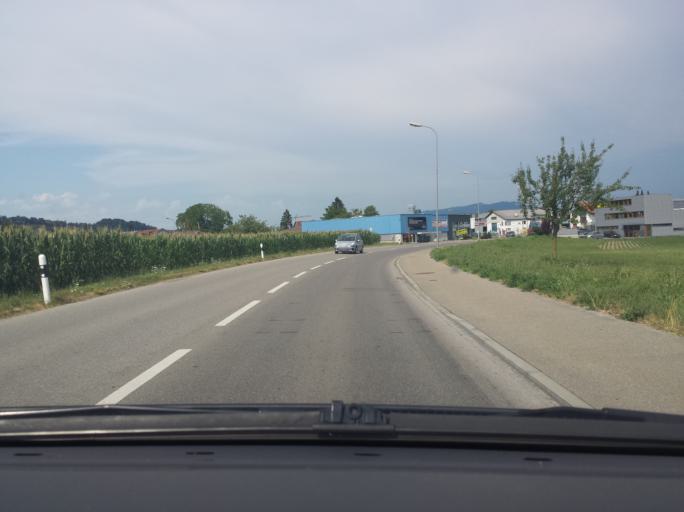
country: CH
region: Saint Gallen
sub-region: Wahlkreis Rheintal
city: Au
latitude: 47.4219
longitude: 9.6335
